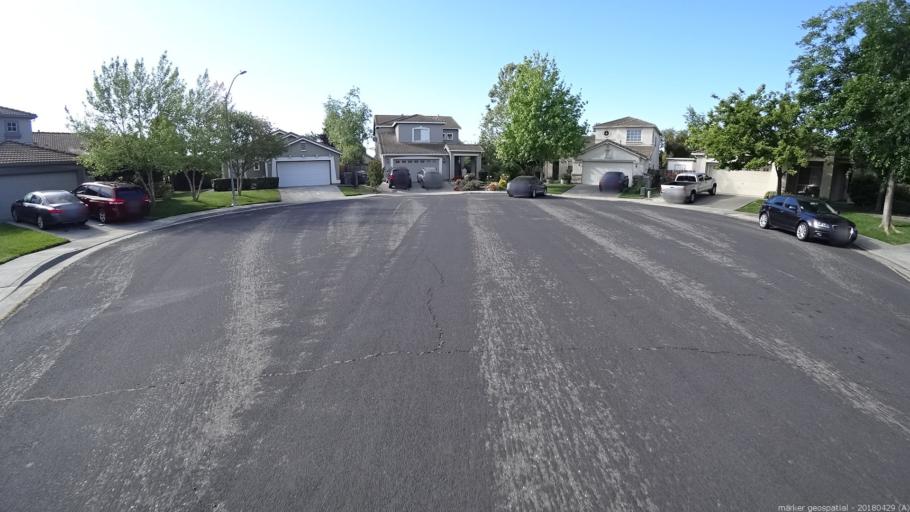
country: US
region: California
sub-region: Yolo County
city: West Sacramento
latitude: 38.5406
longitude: -121.5654
